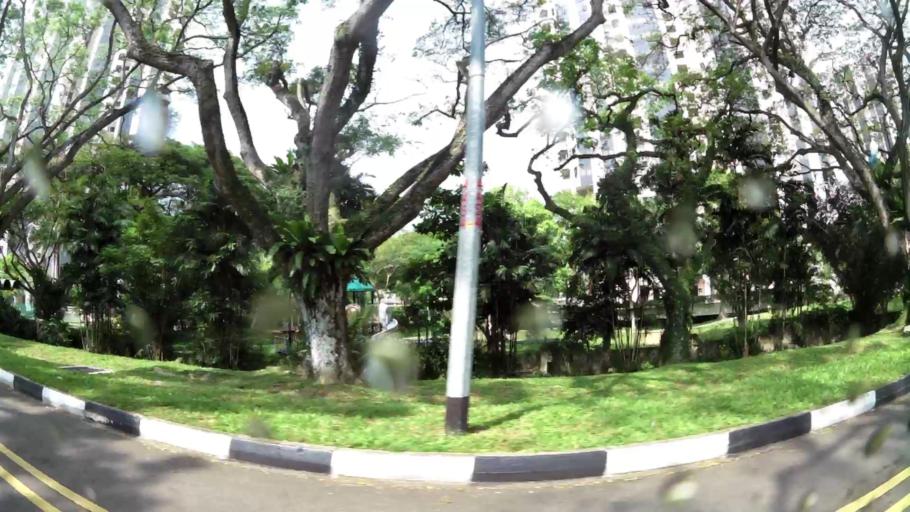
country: SG
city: Singapore
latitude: 1.3105
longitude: 103.9359
